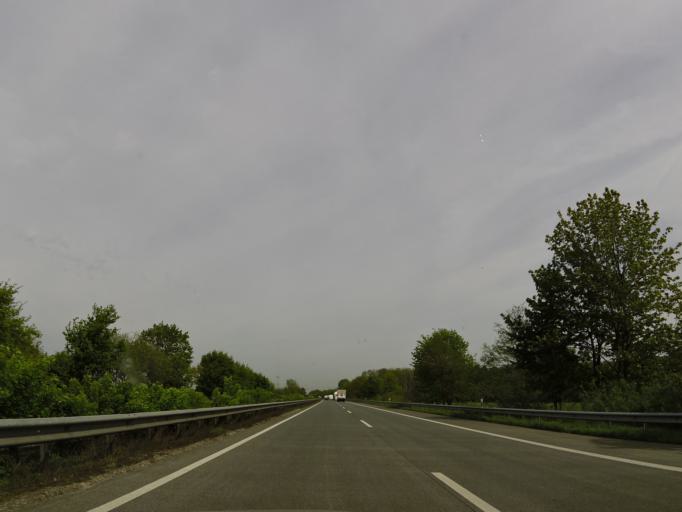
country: DE
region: Schleswig-Holstein
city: Kolln-Reisiek
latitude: 53.7686
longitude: 9.7074
